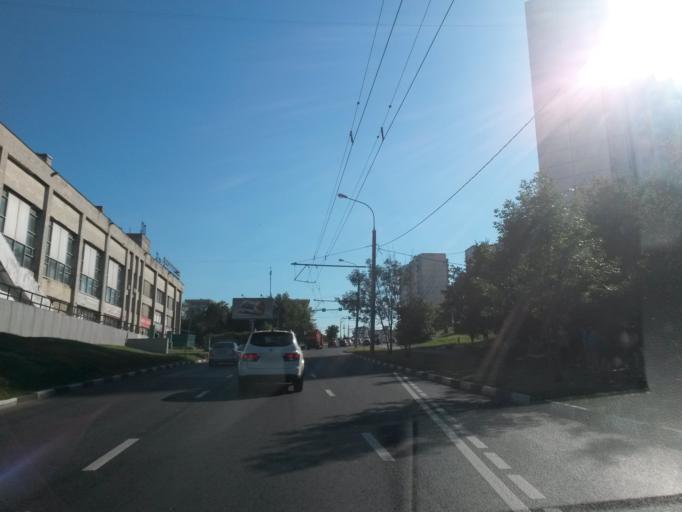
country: RU
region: Moscow
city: Yasenevo
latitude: 55.6145
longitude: 37.5387
